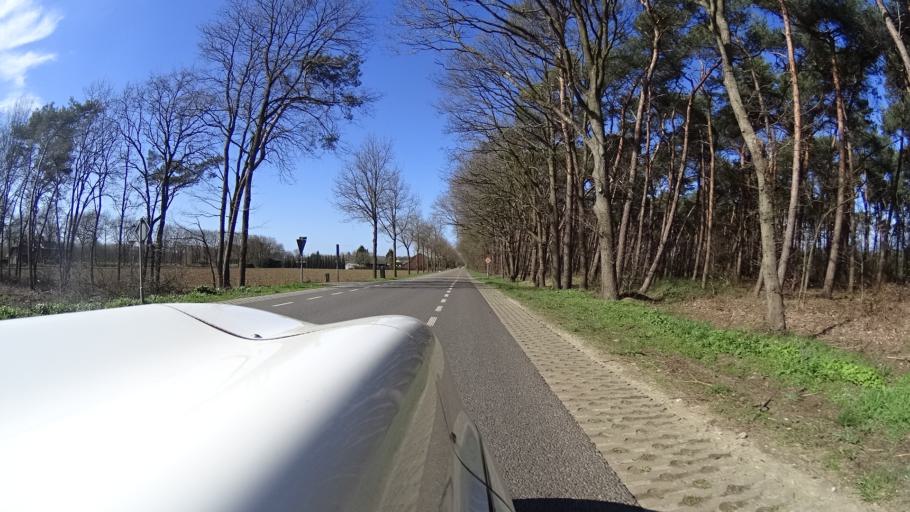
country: NL
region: Limburg
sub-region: Gemeente Bergen
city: Wellerlooi
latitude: 51.5175
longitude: 6.1271
